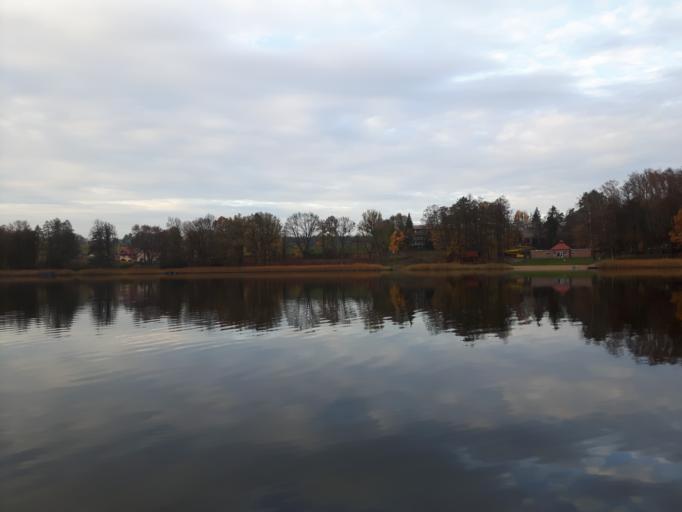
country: PL
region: Warmian-Masurian Voivodeship
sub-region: Powiat olsztynski
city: Barczewo
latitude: 53.8274
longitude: 20.7374
